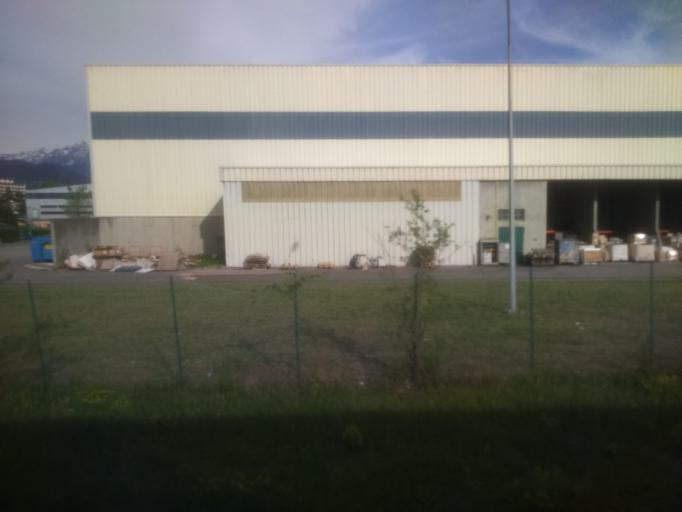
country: FR
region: Rhone-Alpes
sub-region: Departement de l'Isere
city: Le Pont-de-Claix
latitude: 45.1348
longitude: 5.7021
